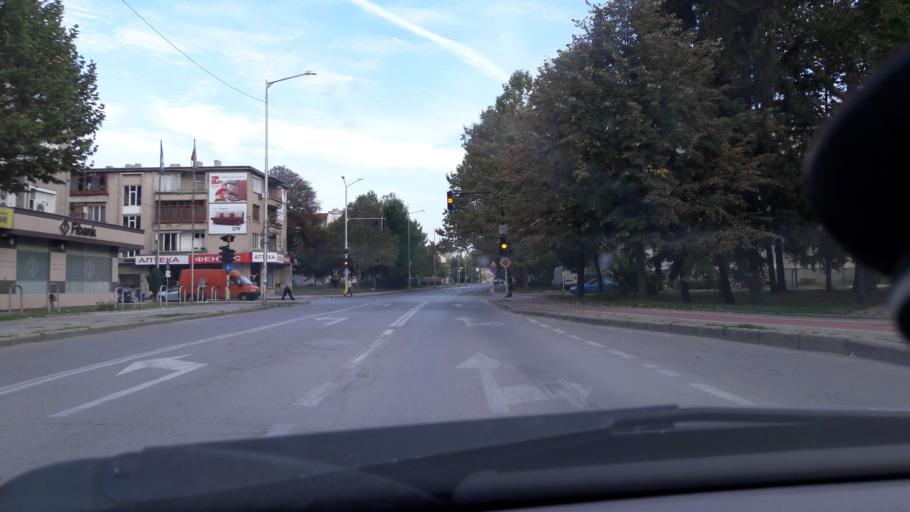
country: BG
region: Razgrad
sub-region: Obshtina Razgrad
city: Razgrad
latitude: 43.5284
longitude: 26.5232
